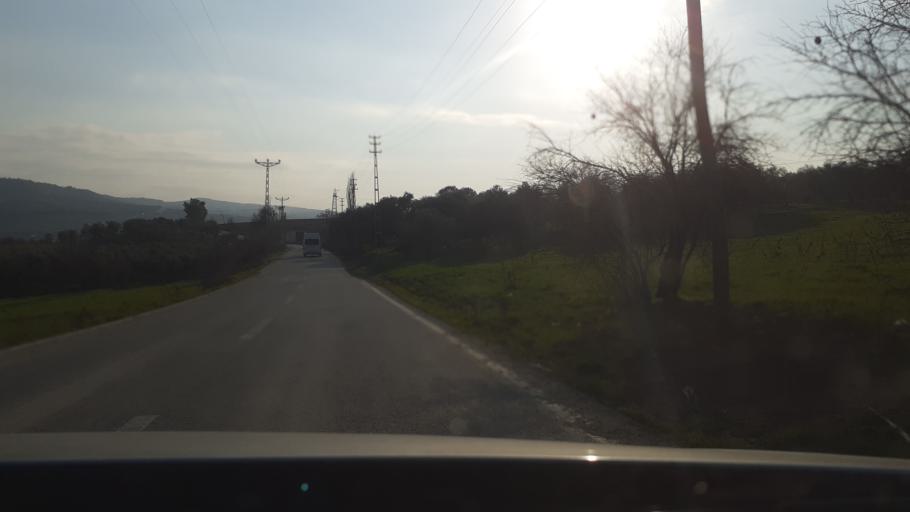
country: TR
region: Hatay
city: Boynuyogun
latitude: 36.1347
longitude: 36.3125
